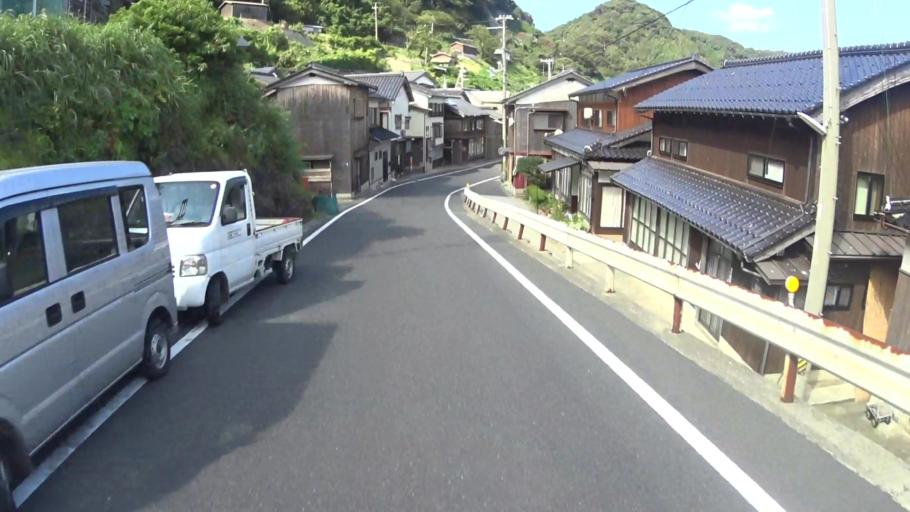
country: JP
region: Kyoto
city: Miyazu
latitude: 35.7512
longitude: 135.2494
